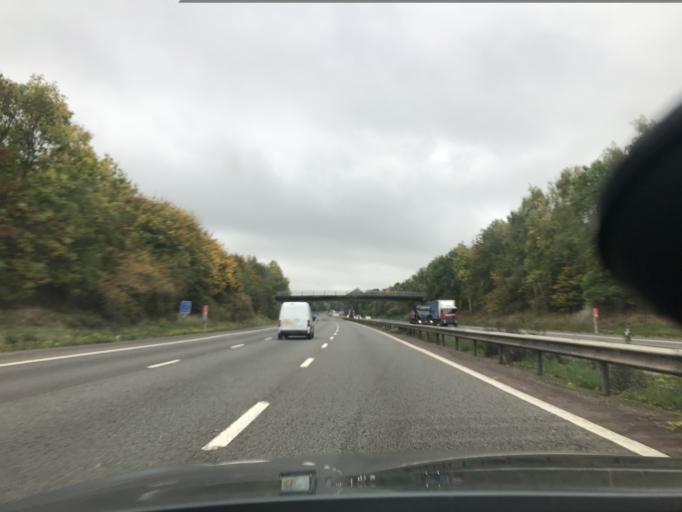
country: GB
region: England
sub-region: Warwickshire
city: Wroxall
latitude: 52.3094
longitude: -1.7080
